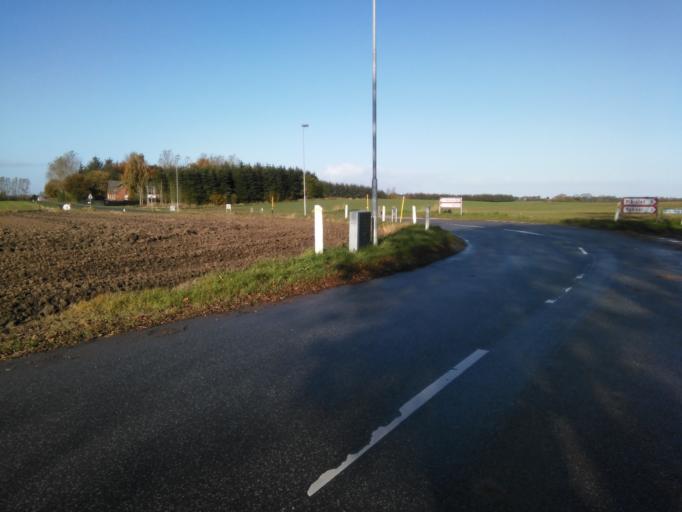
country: DK
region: Central Jutland
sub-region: Arhus Kommune
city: Solbjerg
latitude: 56.0325
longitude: 10.1251
